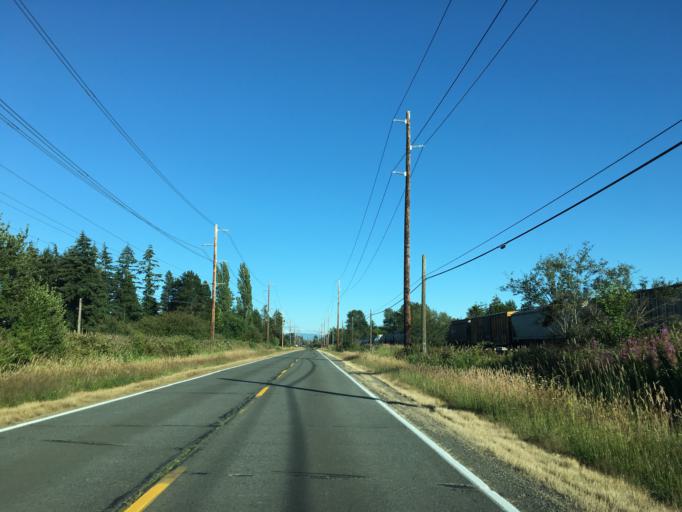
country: US
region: Washington
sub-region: Whatcom County
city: Birch Bay
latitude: 48.9254
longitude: -122.6526
